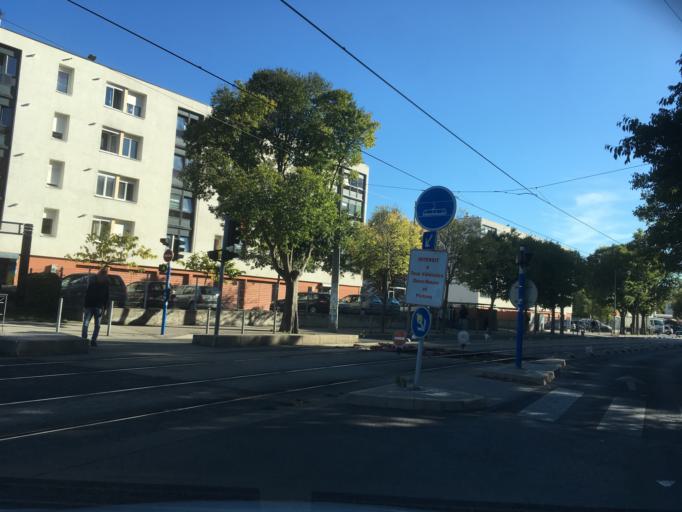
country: FR
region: Languedoc-Roussillon
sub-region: Departement de l'Herault
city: Juvignac
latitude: 43.6270
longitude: 3.8175
